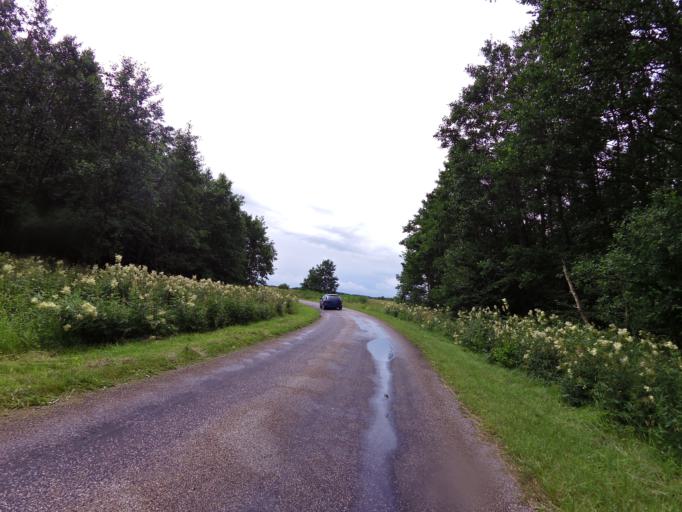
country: EE
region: Laeaene
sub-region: Vormsi vald
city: Hullo
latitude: 58.9888
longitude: 23.3153
